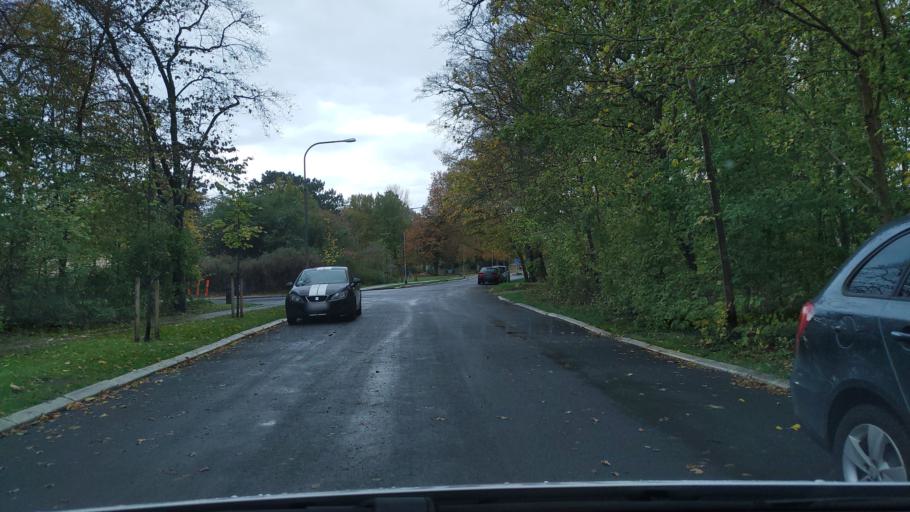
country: DK
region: Capital Region
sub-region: Dragor Kommune
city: Dragor
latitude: 55.5906
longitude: 12.6658
